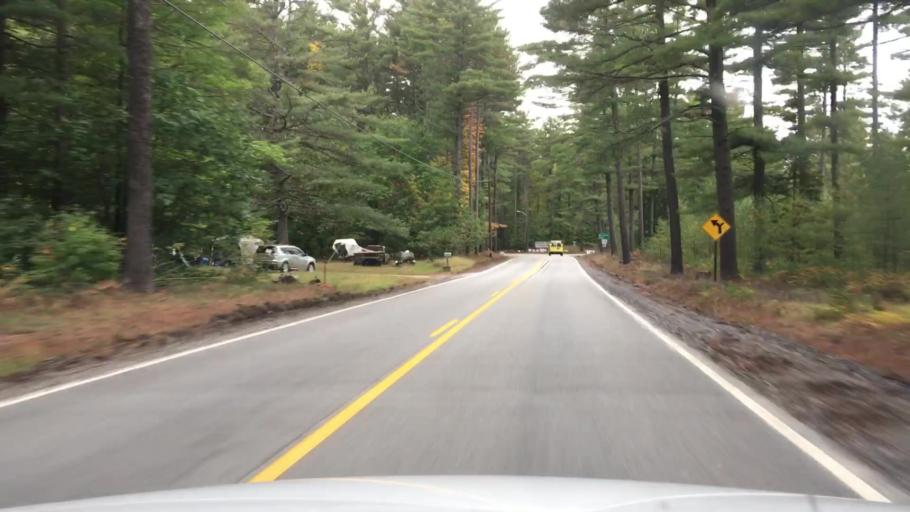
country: US
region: Maine
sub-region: Cumberland County
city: Harrison
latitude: 44.2283
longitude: -70.7034
